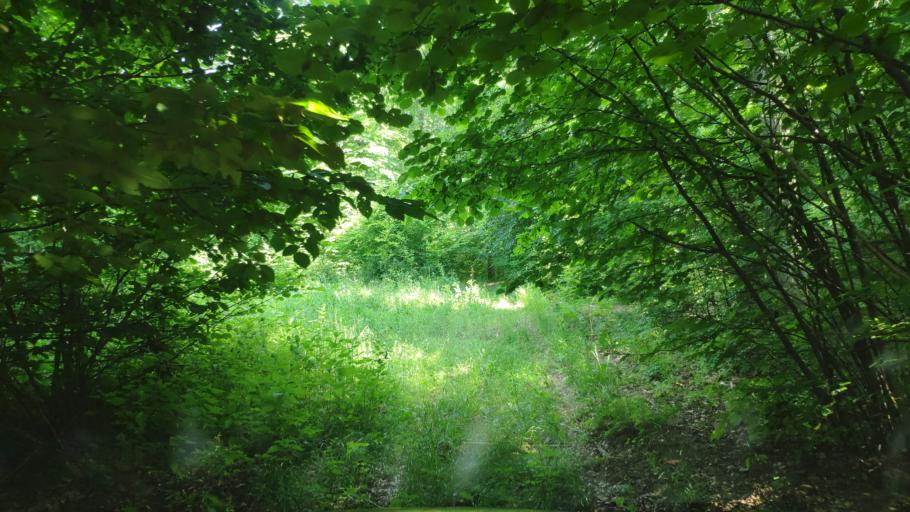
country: SK
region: Presovsky
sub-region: Okres Presov
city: Presov
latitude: 48.9694
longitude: 21.1511
